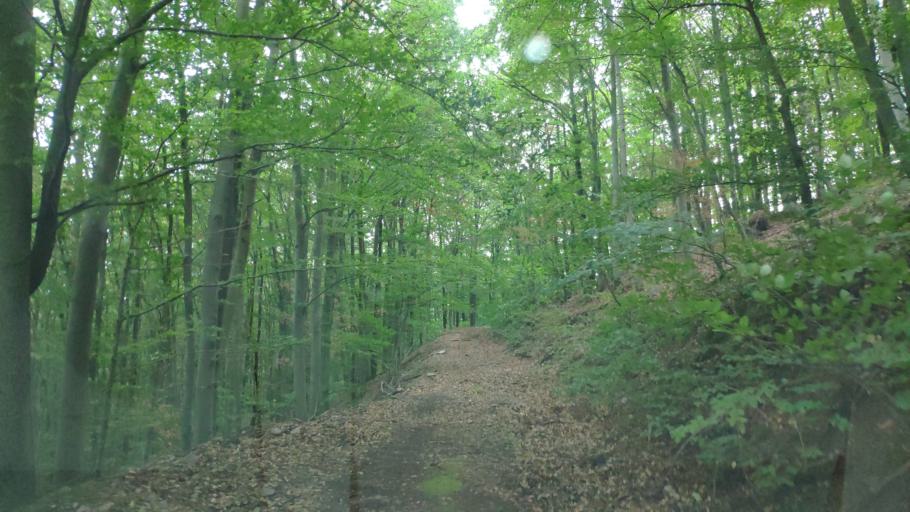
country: SK
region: Presovsky
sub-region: Okres Presov
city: Presov
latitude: 48.8668
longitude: 21.2251
